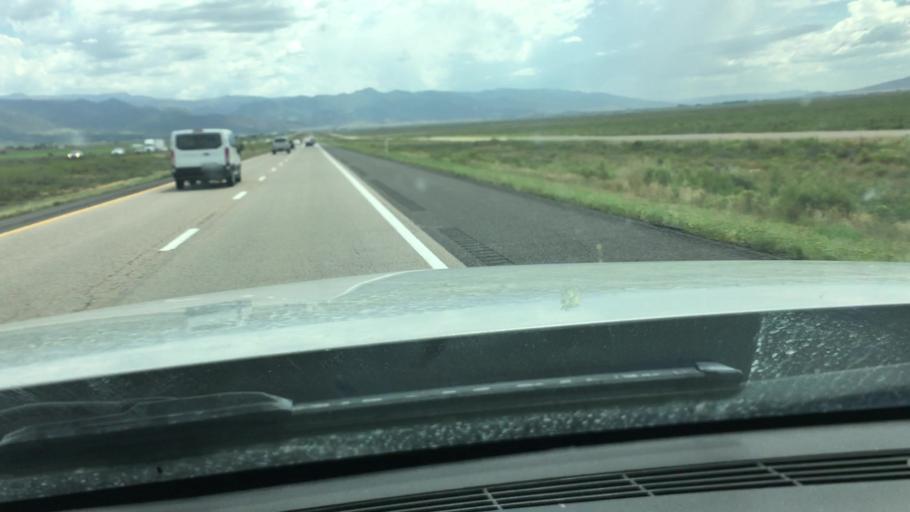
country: US
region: Utah
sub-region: Iron County
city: Parowan
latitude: 37.9505
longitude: -112.7551
